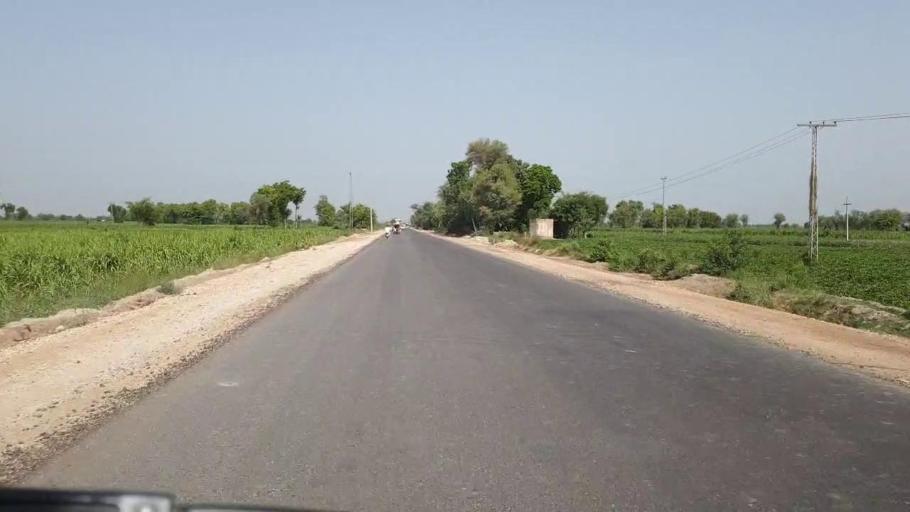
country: PK
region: Sindh
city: Sakrand
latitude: 26.2726
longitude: 68.1575
